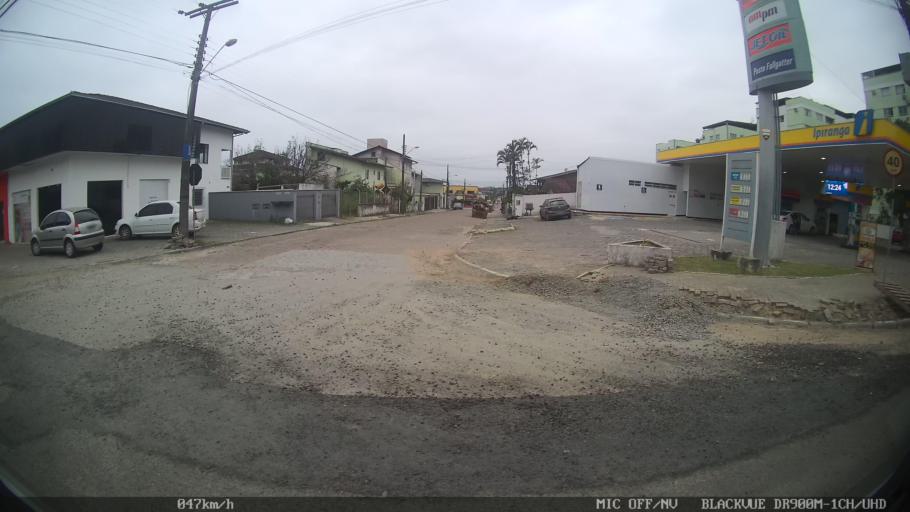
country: BR
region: Santa Catarina
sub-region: Joinville
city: Joinville
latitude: -26.3001
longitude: -48.8231
